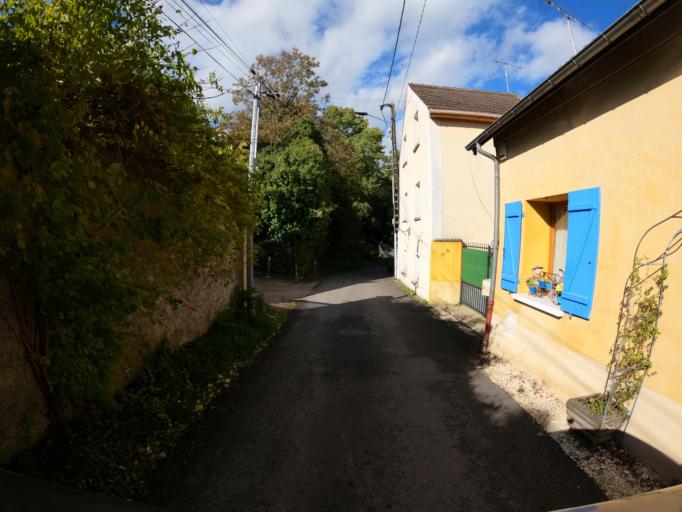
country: FR
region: Ile-de-France
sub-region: Departement de Seine-et-Marne
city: Montry
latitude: 48.8859
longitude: 2.8217
